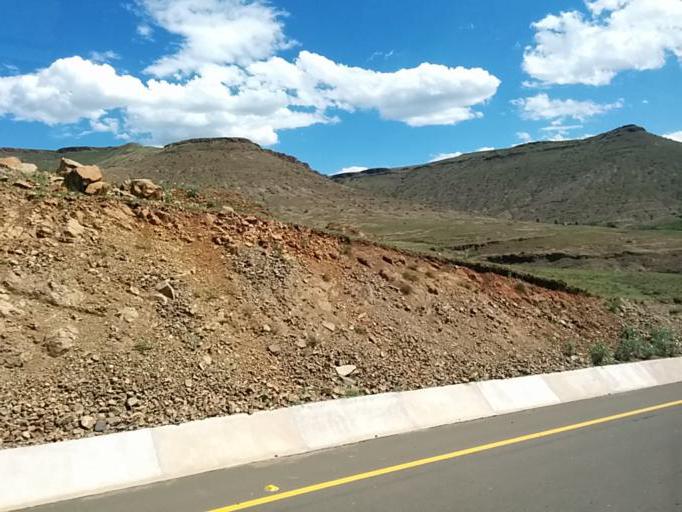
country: LS
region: Maseru
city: Nako
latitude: -29.9875
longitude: 28.1561
